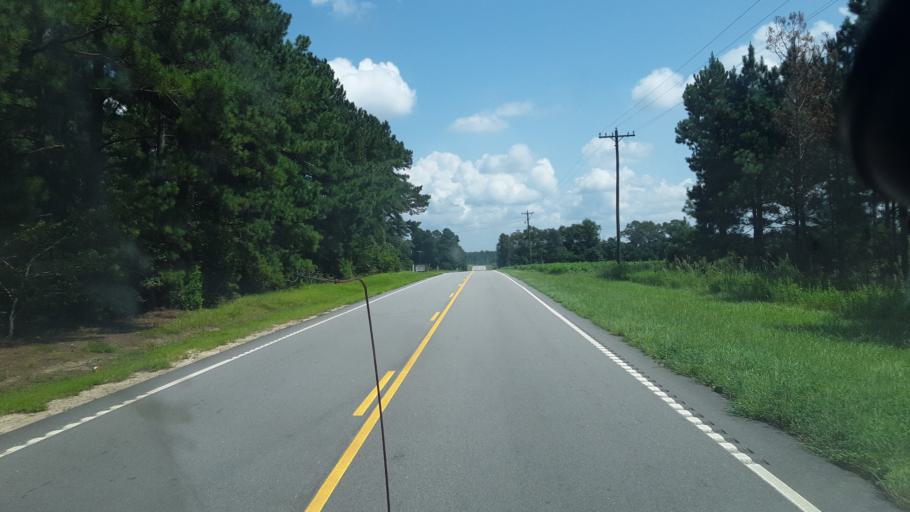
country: US
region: South Carolina
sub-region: Calhoun County
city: Oak Grove
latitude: 33.6596
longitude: -80.9766
